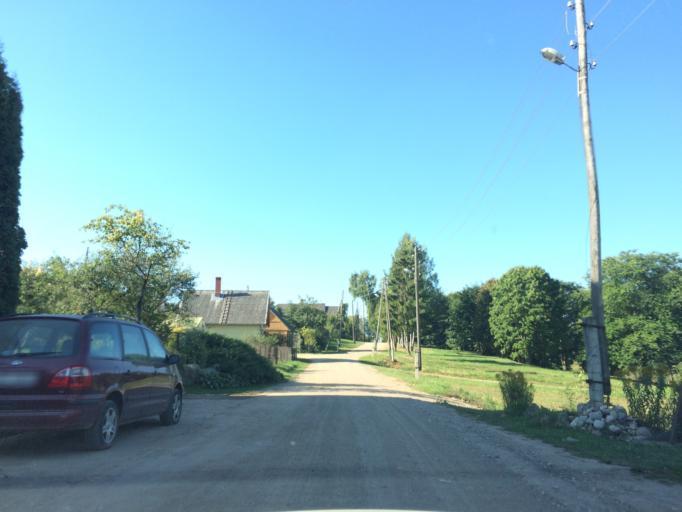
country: LV
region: Rezekne
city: Rezekne
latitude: 56.5108
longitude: 27.3539
